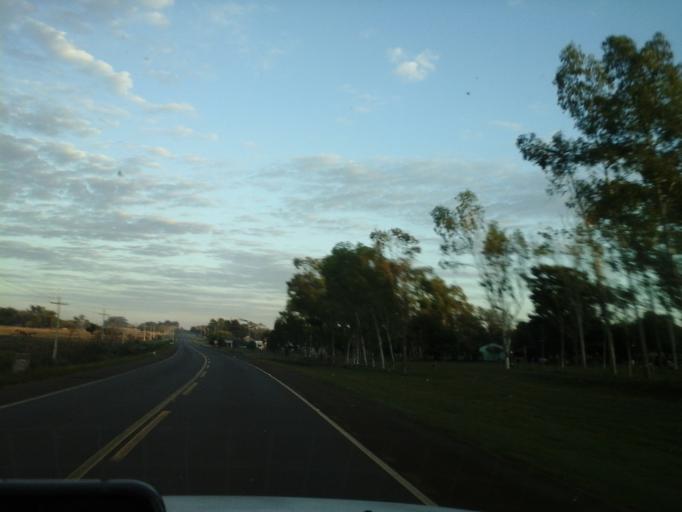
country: PY
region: Misiones
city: Santiago
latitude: -27.0360
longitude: -56.6715
